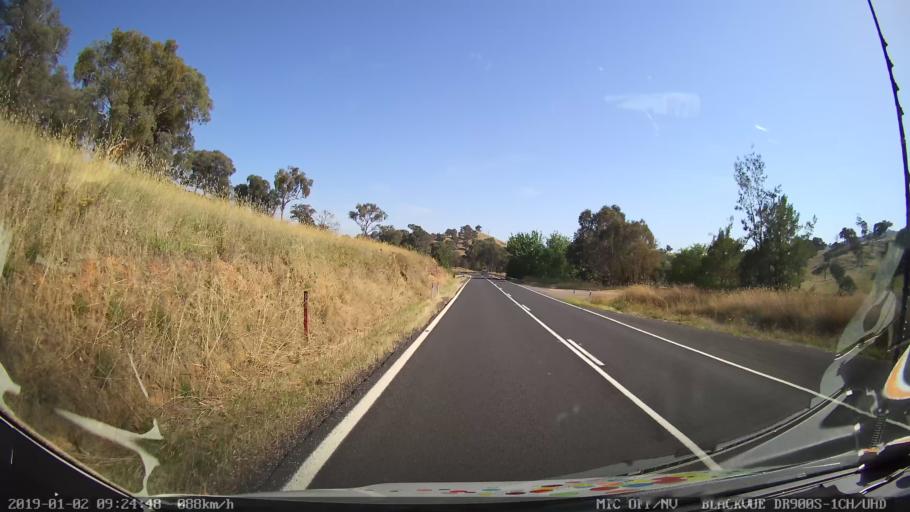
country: AU
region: New South Wales
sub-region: Tumut Shire
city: Tumut
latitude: -35.3721
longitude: 148.2919
